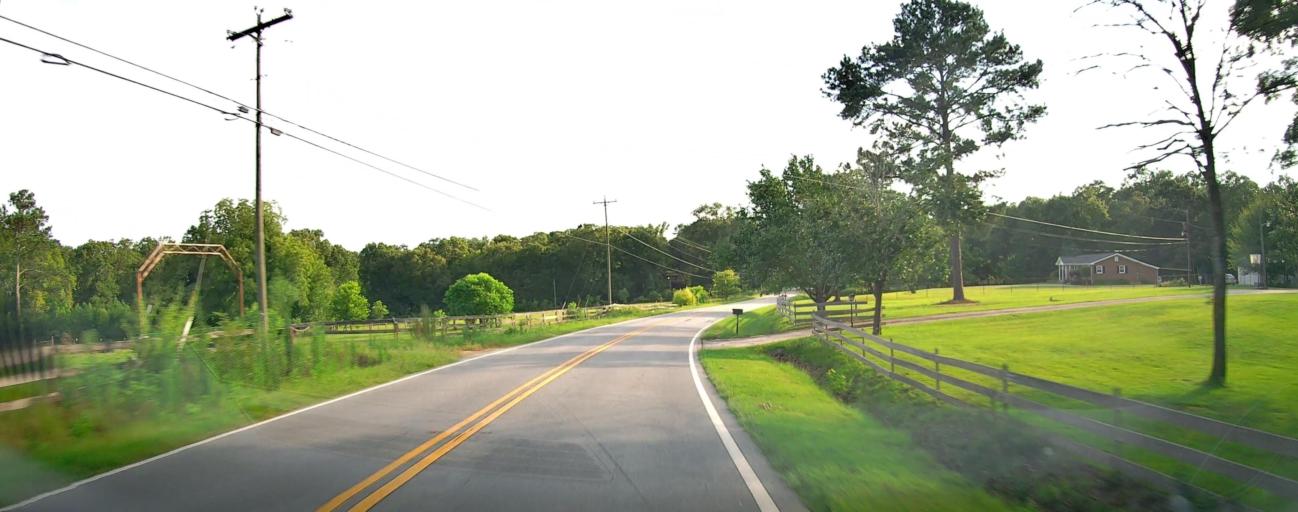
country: US
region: Georgia
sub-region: Peach County
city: Byron
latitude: 32.7366
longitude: -83.7340
